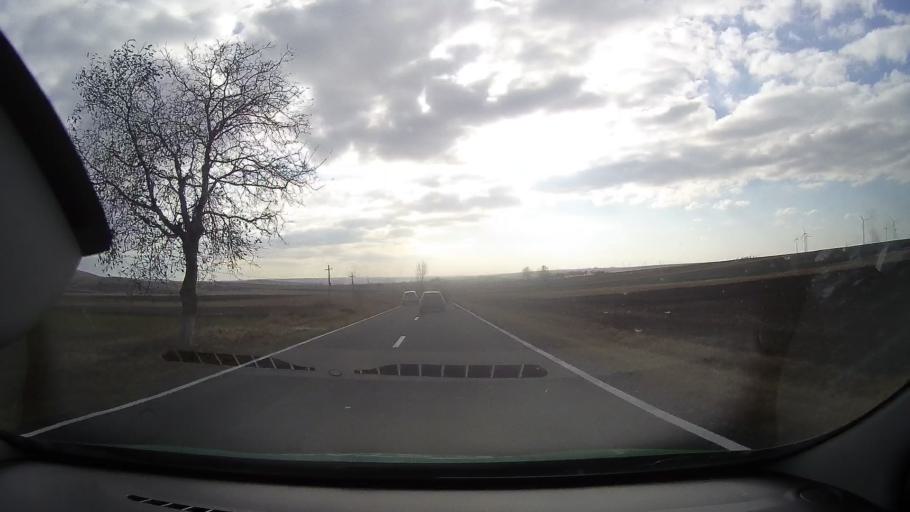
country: RO
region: Tulcea
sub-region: Comuna Topolog
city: Topolog
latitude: 44.8922
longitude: 28.3947
